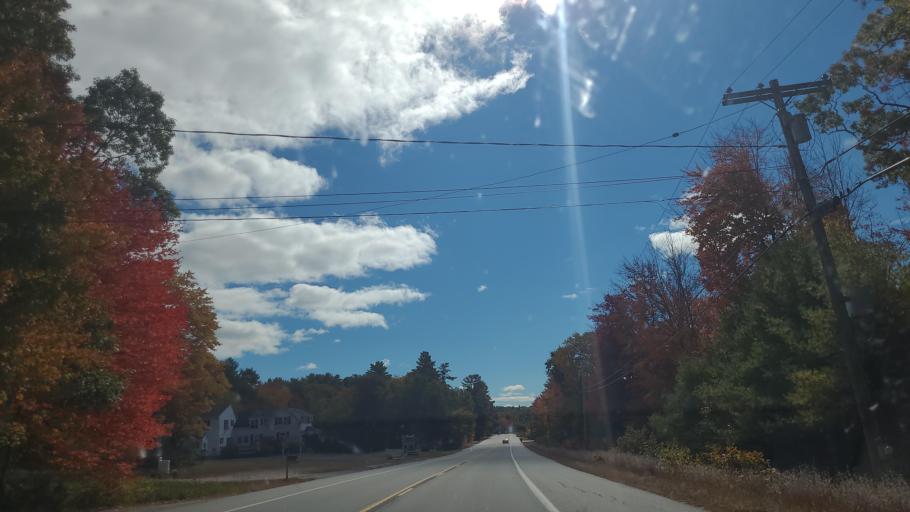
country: US
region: Maine
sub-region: Cumberland County
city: Raymond
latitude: 43.9399
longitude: -70.5442
